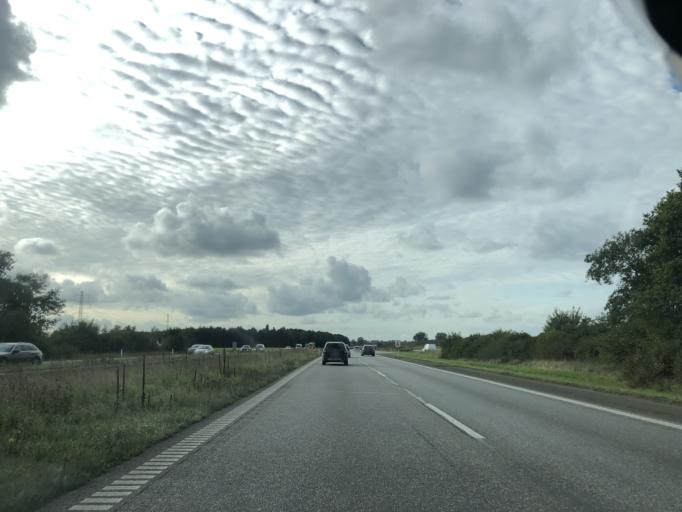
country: DK
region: Zealand
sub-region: Koge Kommune
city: Borup
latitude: 55.4571
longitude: 11.9815
